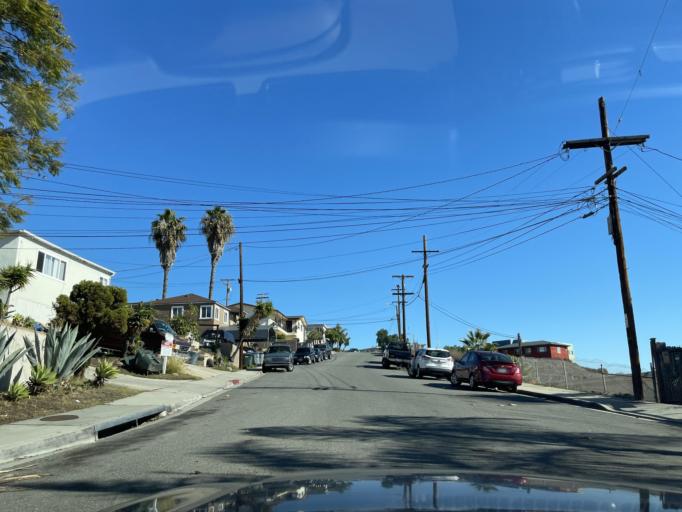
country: US
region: California
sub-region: San Diego County
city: National City
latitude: 32.6779
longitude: -117.0964
